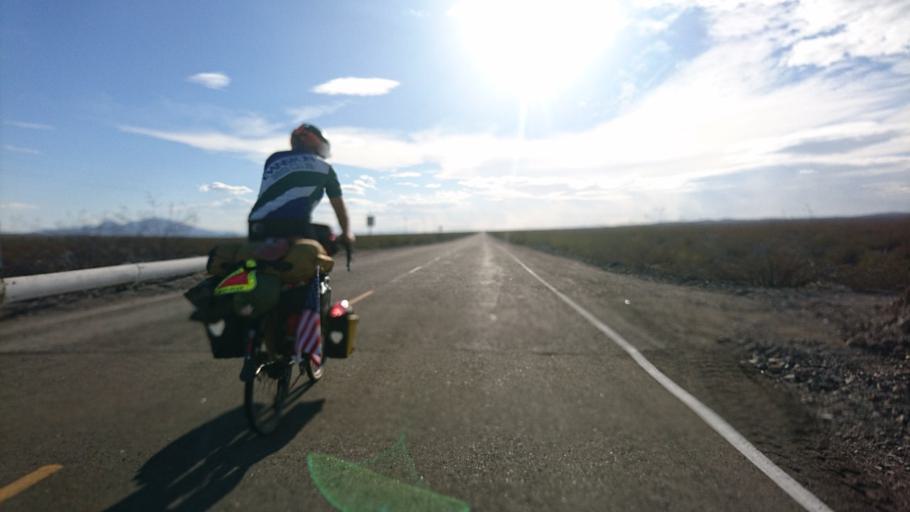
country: US
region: California
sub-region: San Bernardino County
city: Needles
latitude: 34.6892
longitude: -115.3138
